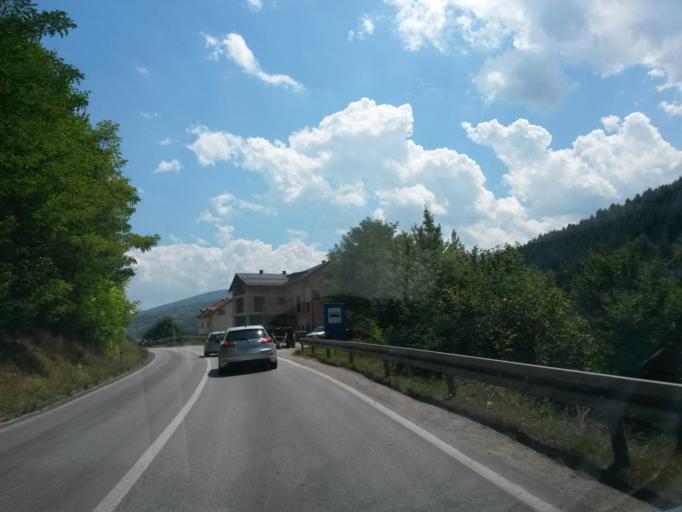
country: BA
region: Federation of Bosnia and Herzegovina
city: Turbe
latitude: 44.2415
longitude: 17.5994
